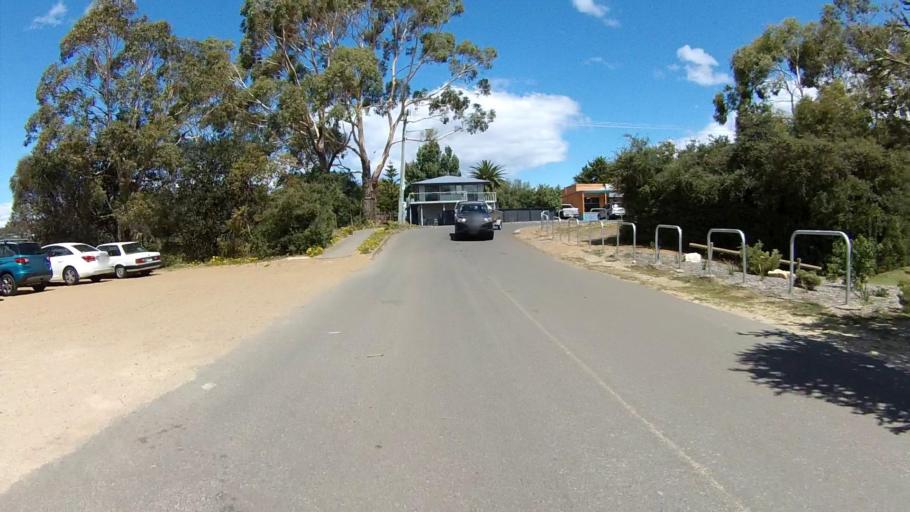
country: AU
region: Tasmania
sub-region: Clarence
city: Lauderdale
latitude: -42.9113
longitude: 147.4949
